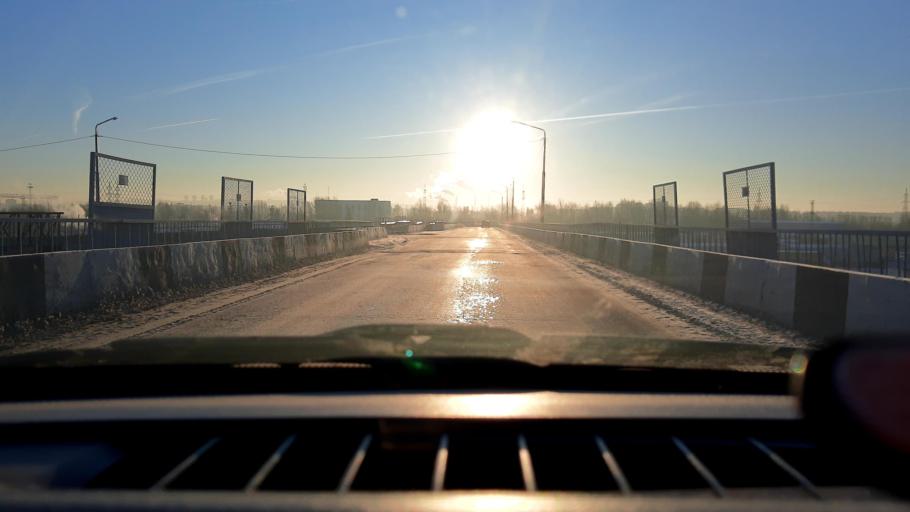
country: RU
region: Nizjnij Novgorod
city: Gorbatovka
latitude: 56.2815
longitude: 43.8424
